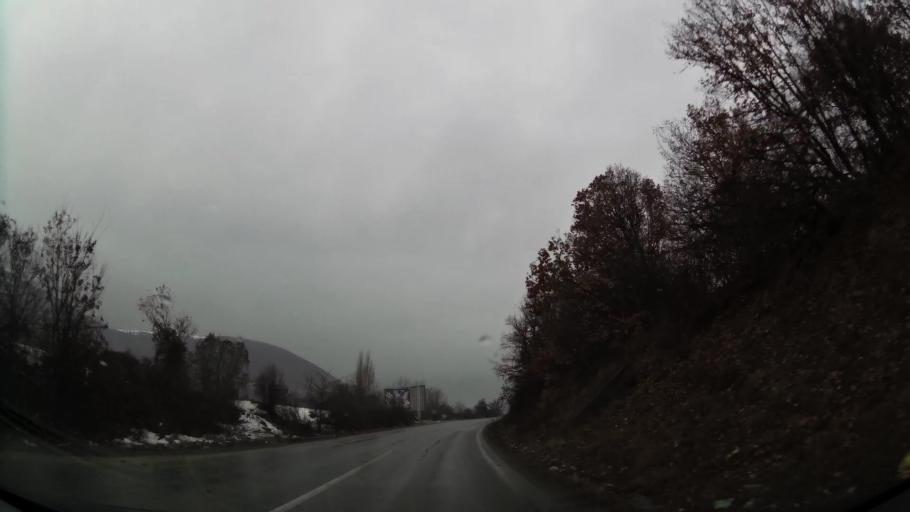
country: XK
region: Ferizaj
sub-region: Hani i Elezit
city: Hani i Elezit
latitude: 42.1337
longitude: 21.3092
